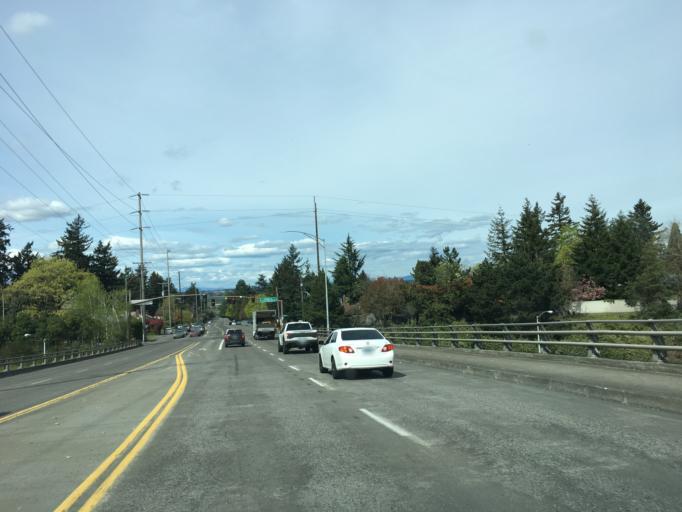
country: US
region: Oregon
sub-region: Multnomah County
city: Lents
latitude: 45.5472
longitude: -122.5578
